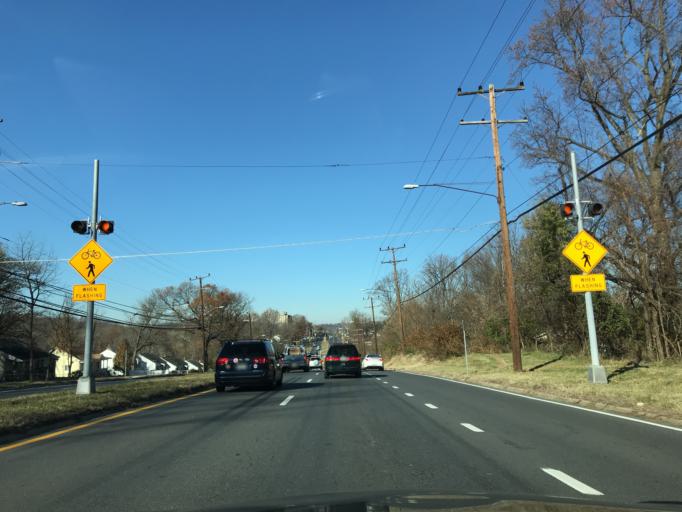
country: US
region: Maryland
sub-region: Montgomery County
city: Aspen Hill
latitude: 39.0586
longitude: -77.0867
